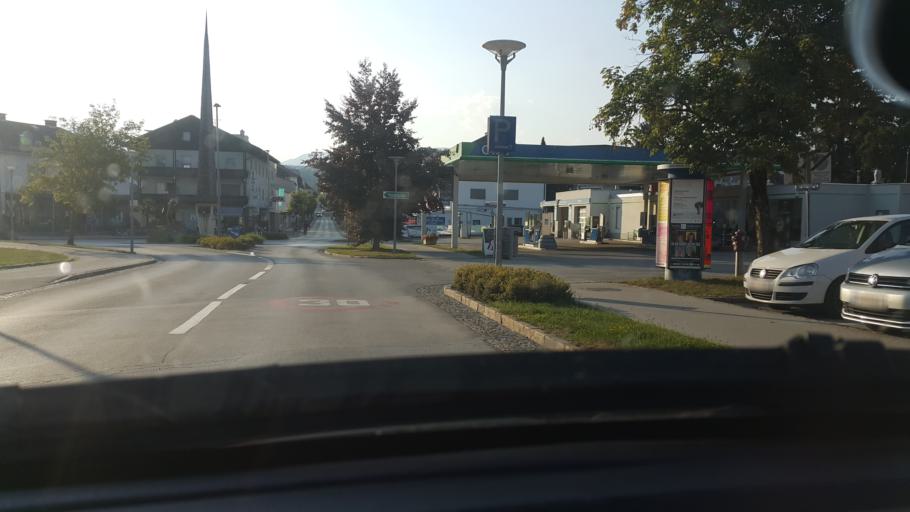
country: AT
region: Carinthia
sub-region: Politischer Bezirk Feldkirchen
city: Feldkirchen in Karnten
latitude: 46.7226
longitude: 14.0971
